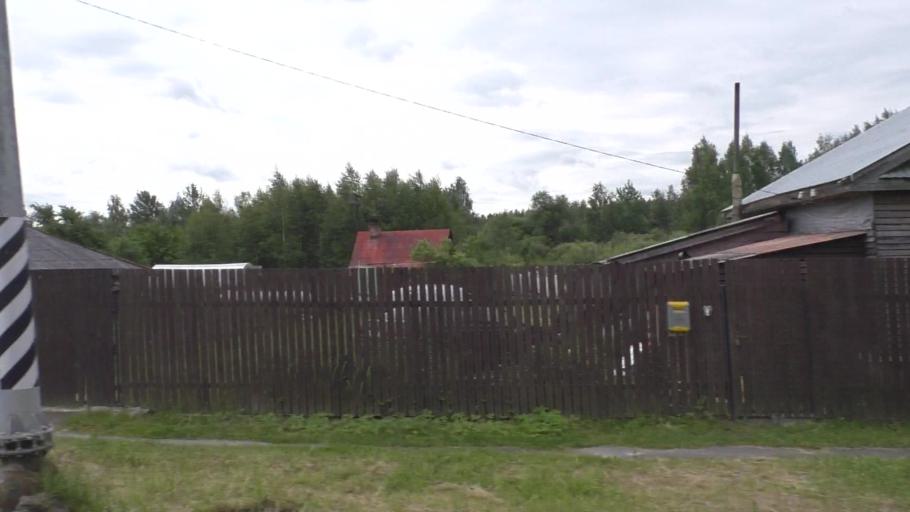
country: RU
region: Moskovskaya
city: Imeni Tsyurupy
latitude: 55.5219
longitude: 38.6932
